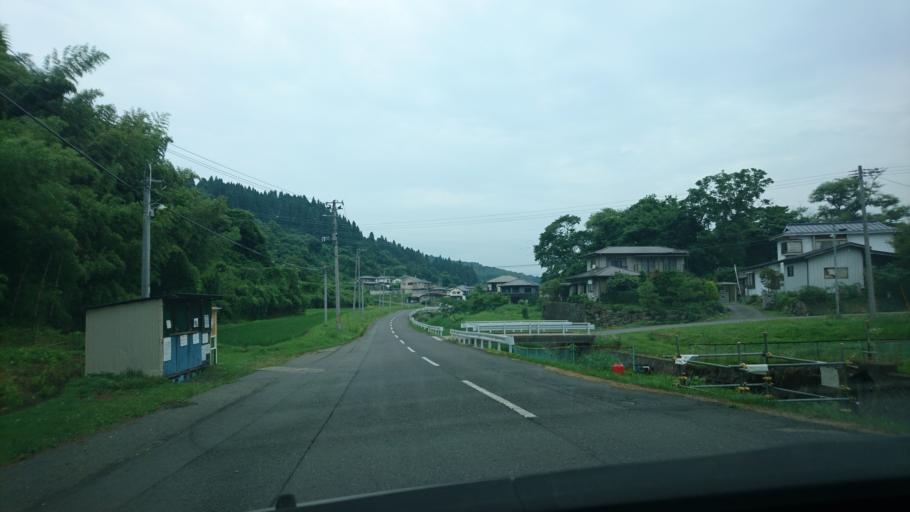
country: JP
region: Iwate
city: Ichinoseki
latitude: 38.9068
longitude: 141.1187
